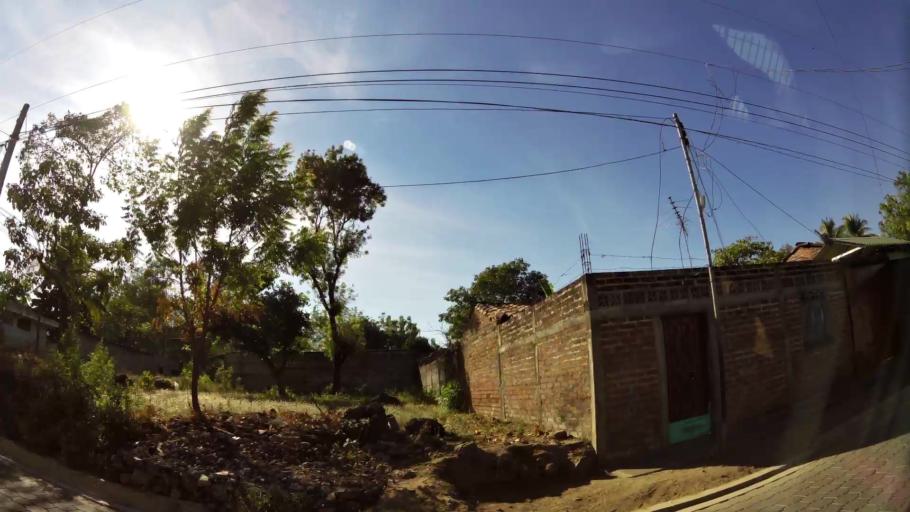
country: SV
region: San Miguel
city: San Miguel
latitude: 13.4753
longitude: -88.1938
